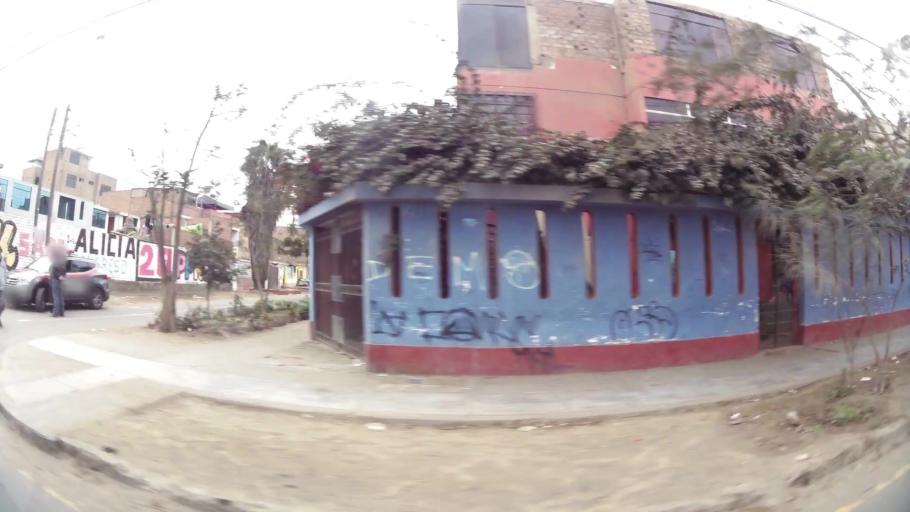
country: PE
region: Lima
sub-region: Lima
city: Independencia
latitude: -11.9754
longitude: -77.0077
